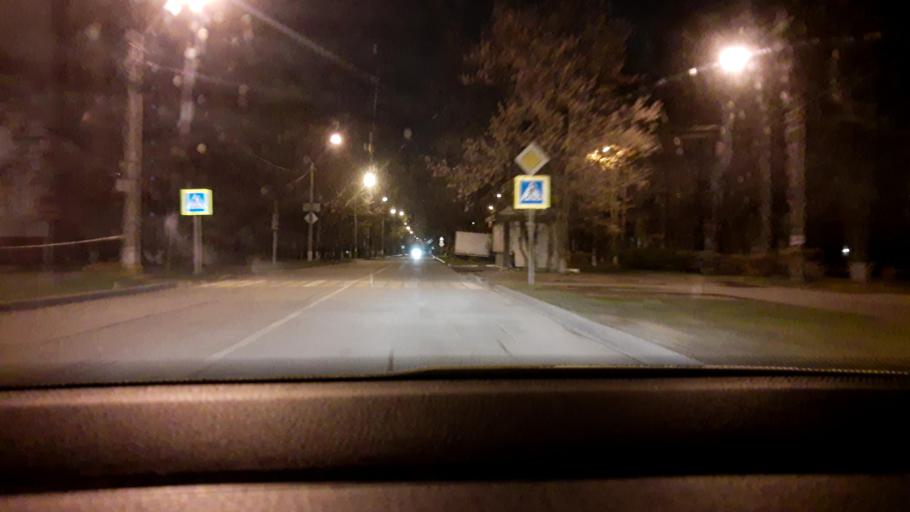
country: RU
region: Moskovskaya
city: Yubileyny
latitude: 55.9328
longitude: 37.8511
